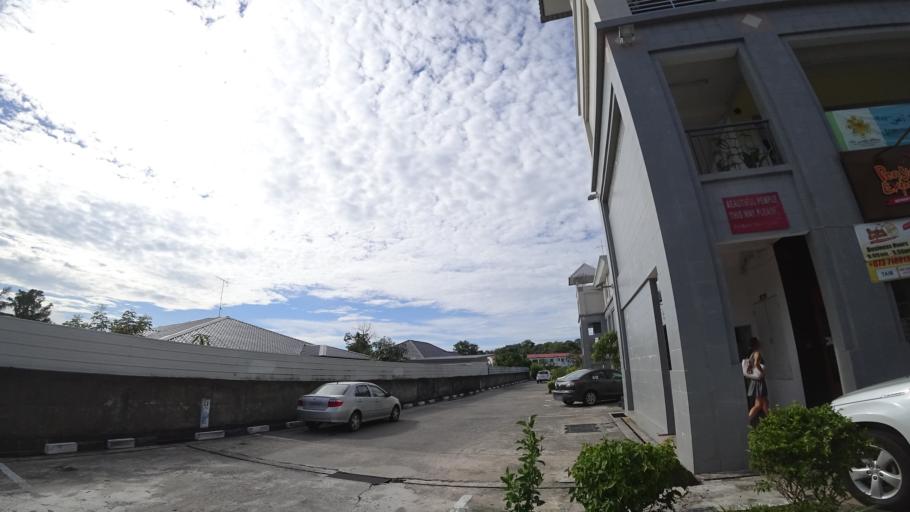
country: BN
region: Brunei and Muara
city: Bandar Seri Begawan
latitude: 4.8907
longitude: 114.8562
